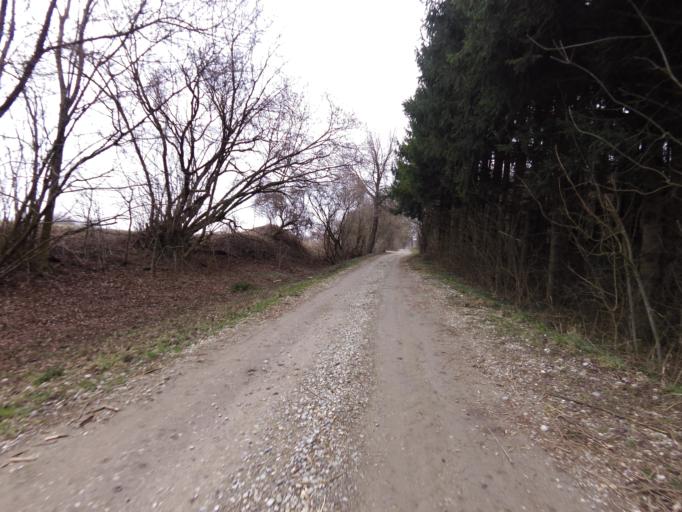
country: DE
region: Bavaria
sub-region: Upper Bavaria
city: Langenpreising
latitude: 48.4332
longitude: 11.9886
